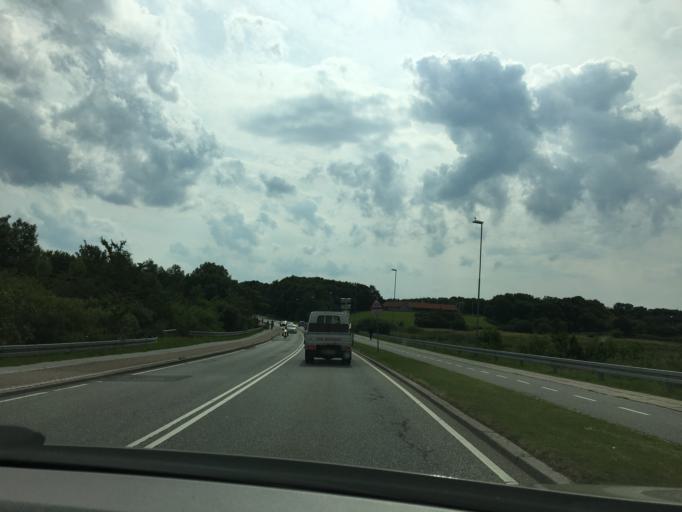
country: DK
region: Central Jutland
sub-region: Skive Kommune
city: Skive
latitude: 56.5595
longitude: 9.0253
